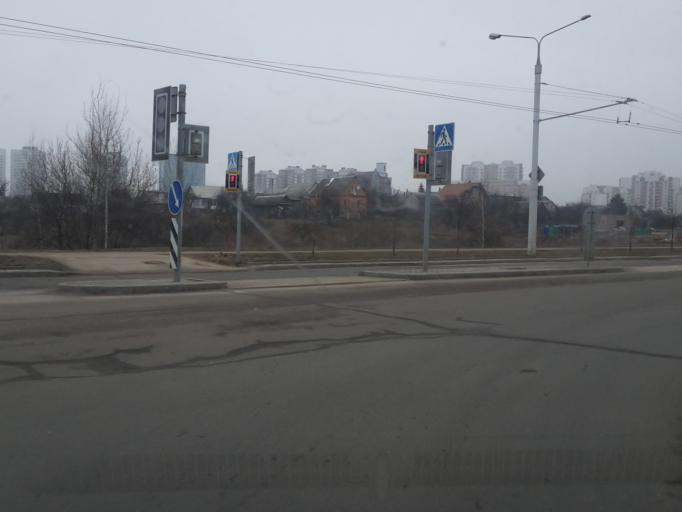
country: BY
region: Minsk
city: Novoye Medvezhino
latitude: 53.9012
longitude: 27.4238
